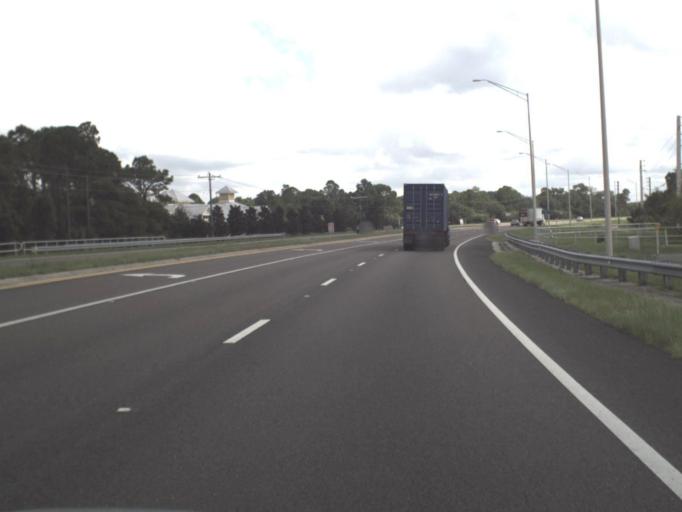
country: US
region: Florida
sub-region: Manatee County
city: Ellenton
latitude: 27.4831
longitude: -82.4076
